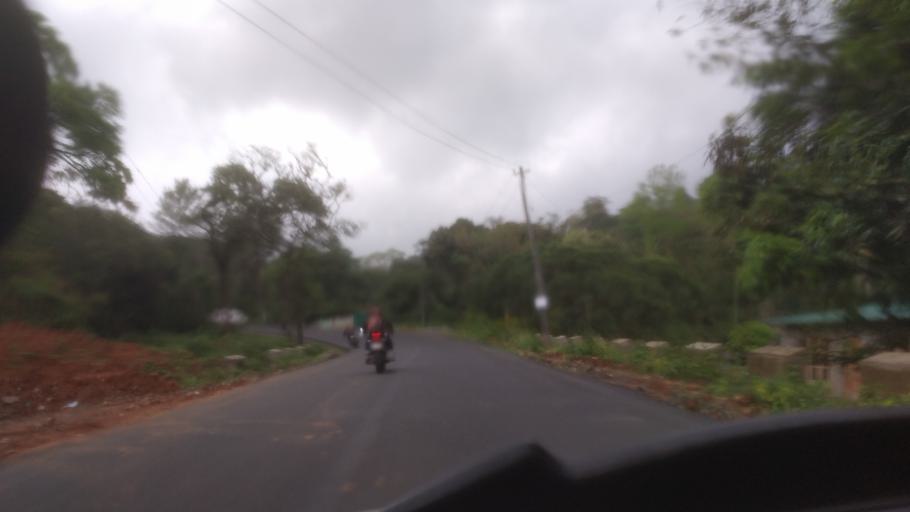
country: IN
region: Tamil Nadu
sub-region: Theni
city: Kombai
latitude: 9.8907
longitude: 77.1498
